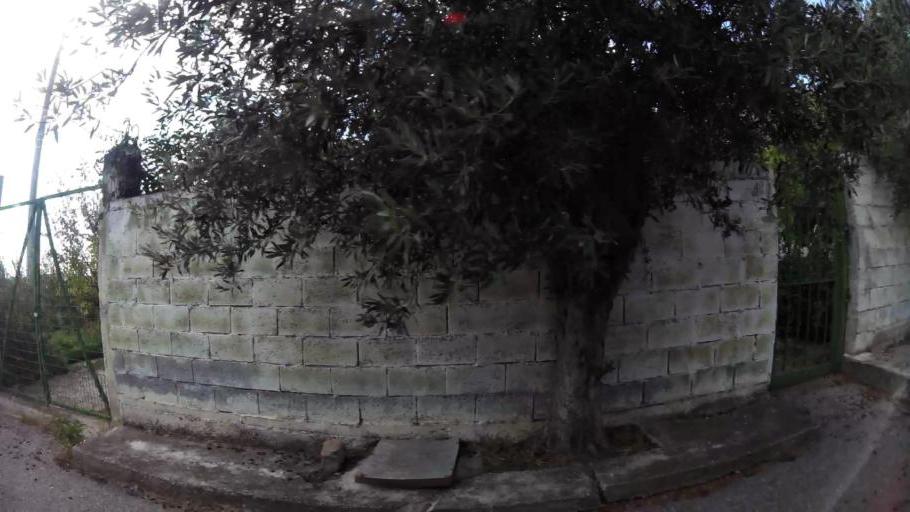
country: GR
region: Attica
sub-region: Nomarchia Anatolikis Attikis
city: Thrakomakedones
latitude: 38.1185
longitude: 23.7319
